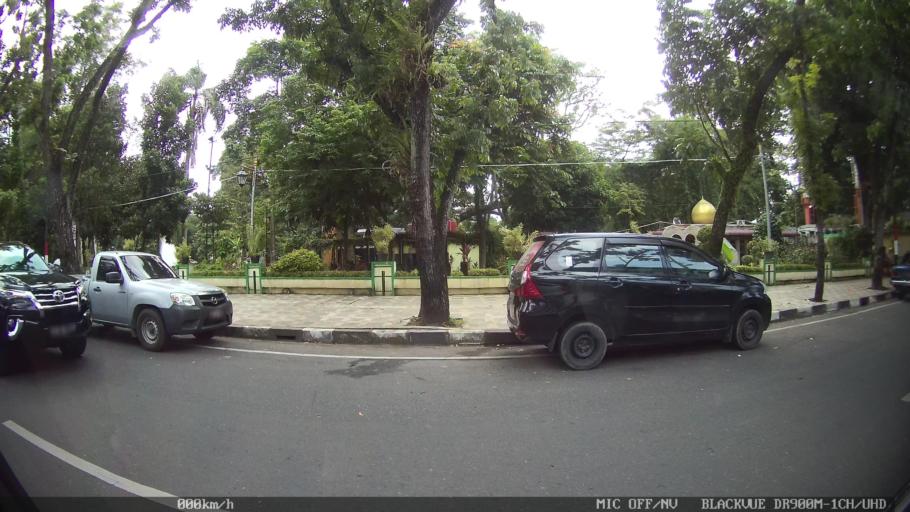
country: ID
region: North Sumatra
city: Medan
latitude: 3.5767
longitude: 98.6698
